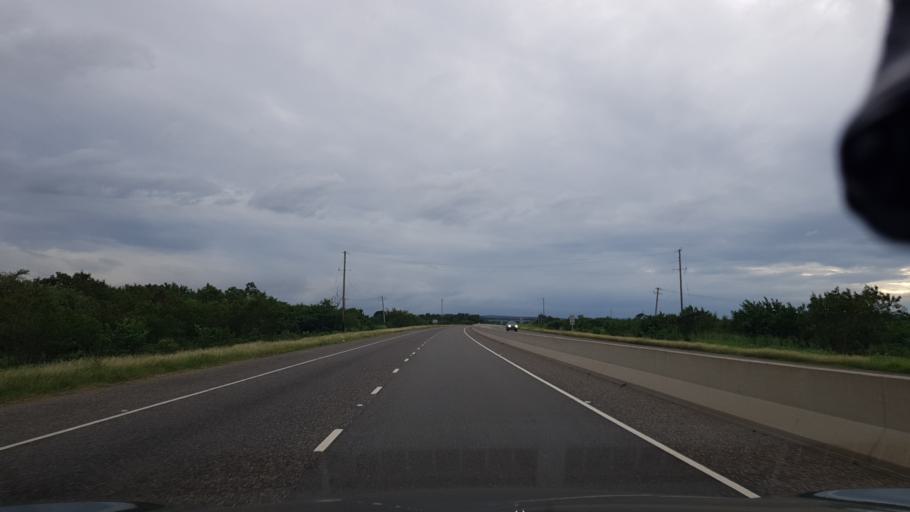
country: JM
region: Saint Catherine
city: Portmore
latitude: 17.9981
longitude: -76.8965
